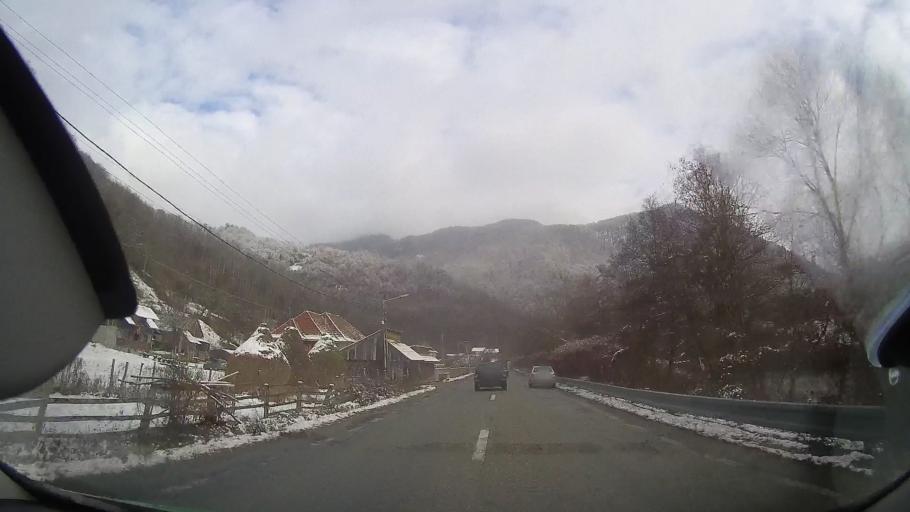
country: RO
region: Alba
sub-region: Oras Baia de Aries
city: Baia de Aries
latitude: 46.4055
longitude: 23.3266
